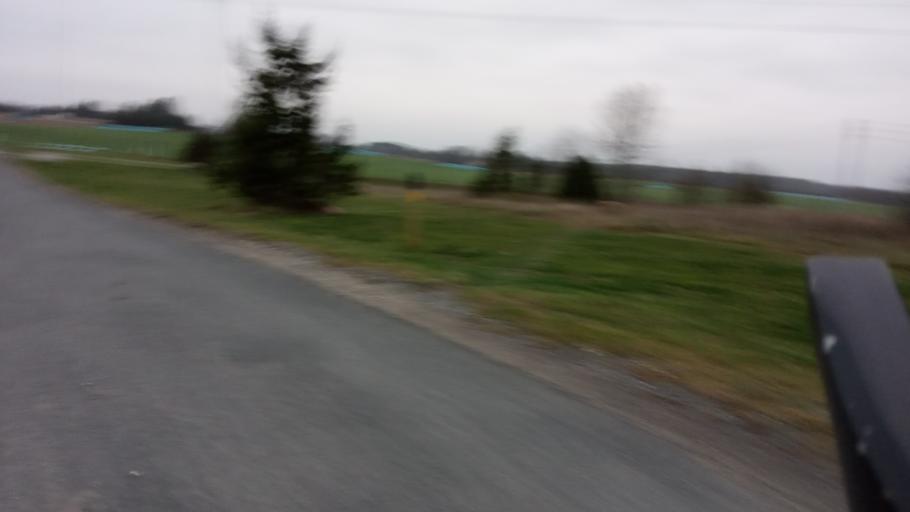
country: EE
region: Harju
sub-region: Kuusalu vald
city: Kuusalu
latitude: 59.4516
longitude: 25.4246
